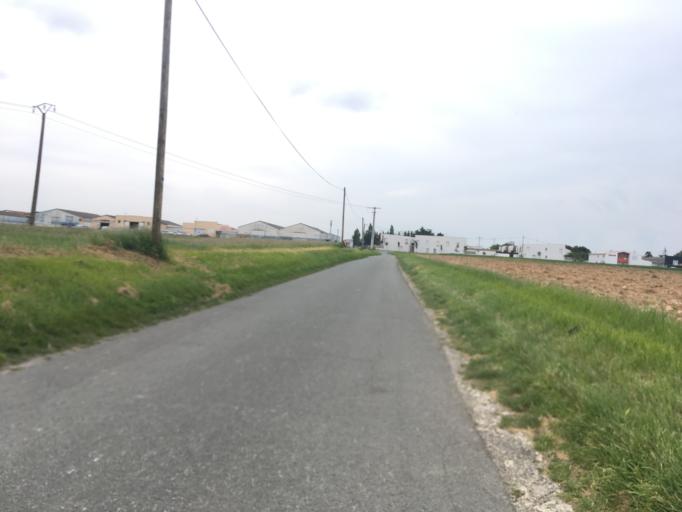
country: FR
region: Poitou-Charentes
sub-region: Departement de la Charente-Maritime
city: Aytre
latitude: 46.1435
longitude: -1.1214
